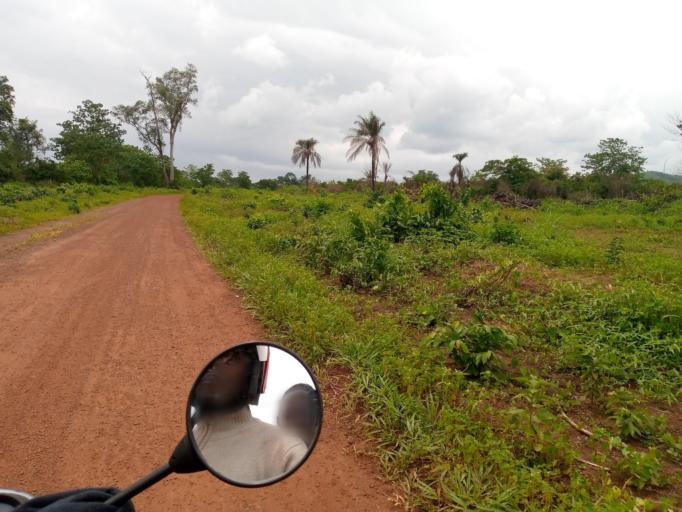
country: SL
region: Southern Province
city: Moyamba
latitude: 8.0821
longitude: -12.4512
